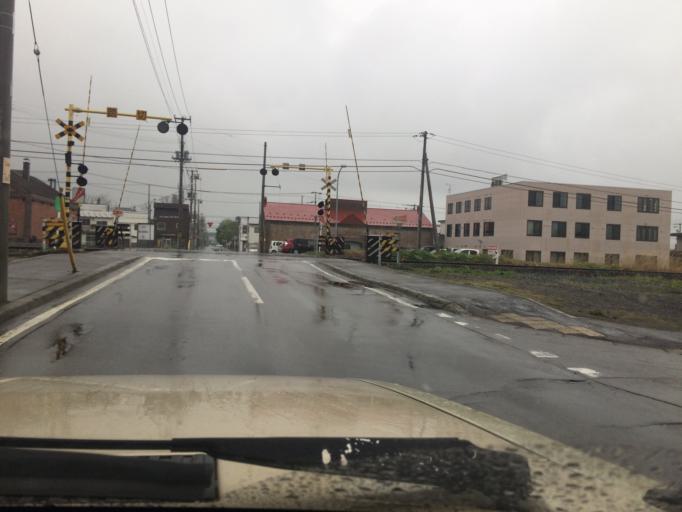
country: JP
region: Hokkaido
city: Obihiro
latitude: 42.9098
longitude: 143.0522
